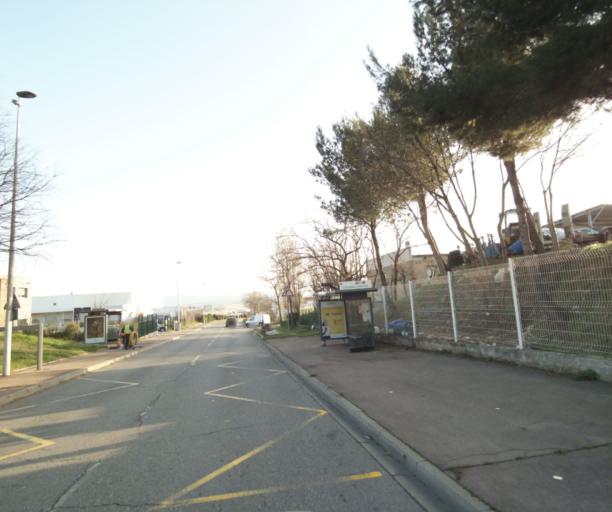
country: FR
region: Provence-Alpes-Cote d'Azur
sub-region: Departement des Bouches-du-Rhone
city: Saint-Victoret
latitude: 43.4340
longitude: 5.2426
